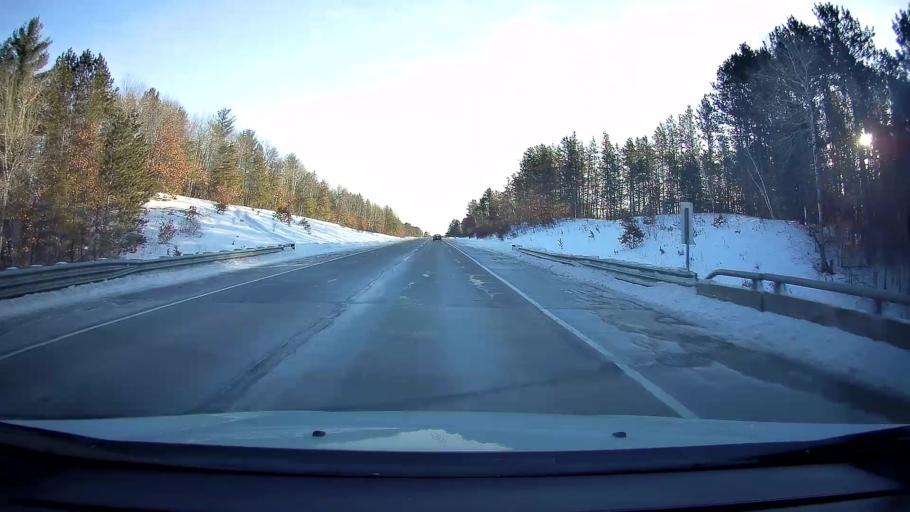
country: US
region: Wisconsin
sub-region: Washburn County
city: Spooner
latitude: 45.9104
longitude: -91.7810
